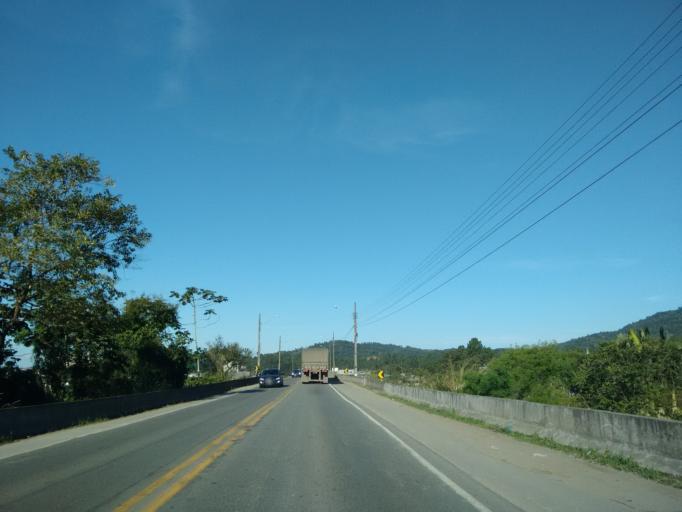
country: BR
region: Santa Catarina
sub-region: Guaramirim
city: Guaramirim
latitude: -26.4763
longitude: -49.0151
